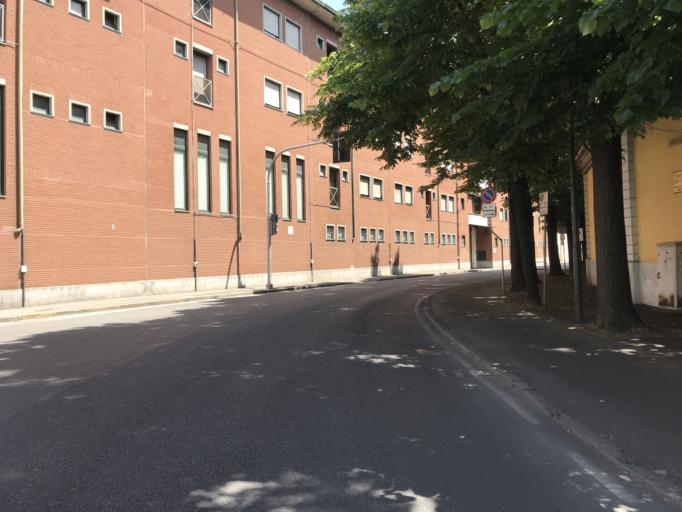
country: IT
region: Emilia-Romagna
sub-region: Provincia di Piacenza
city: Piacenza
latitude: 45.0534
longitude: 9.6825
